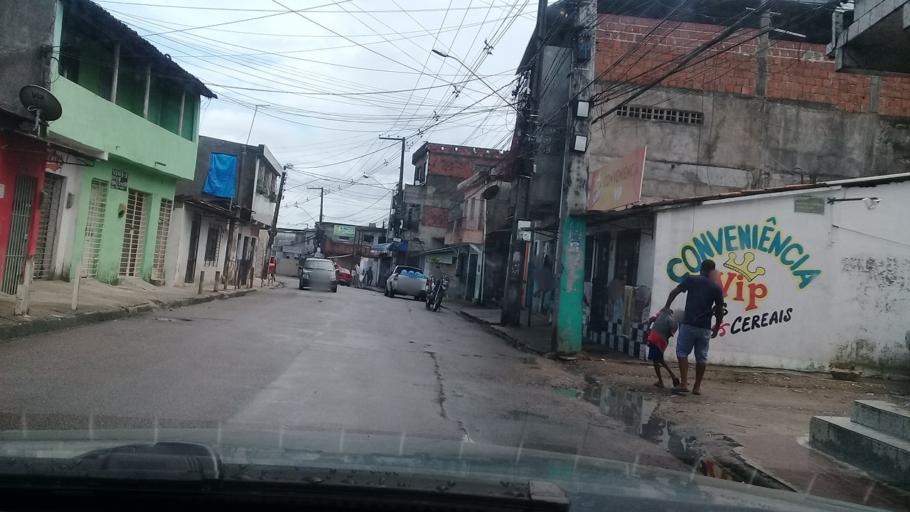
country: BR
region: Pernambuco
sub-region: Jaboatao Dos Guararapes
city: Jaboatao dos Guararapes
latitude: -8.1108
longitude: -34.9590
